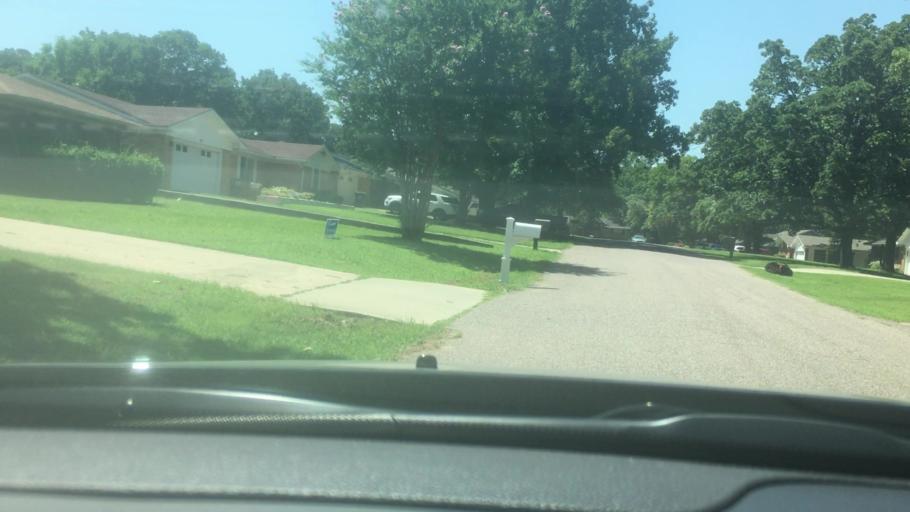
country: US
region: Oklahoma
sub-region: Pontotoc County
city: Ada
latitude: 34.7803
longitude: -96.6381
